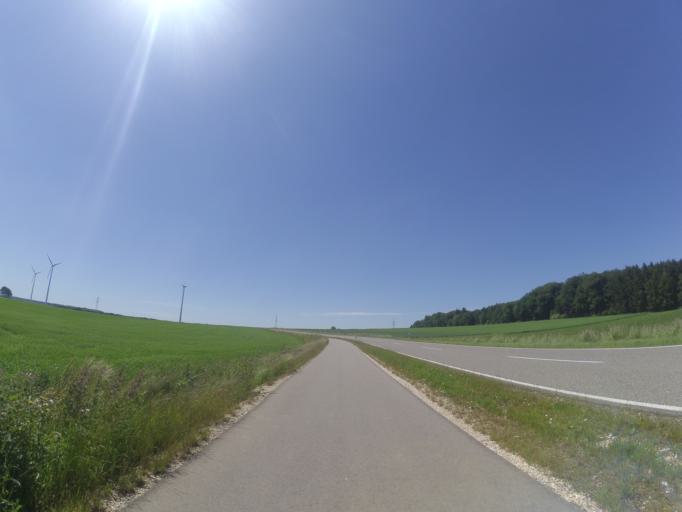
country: DE
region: Baden-Wuerttemberg
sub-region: Tuebingen Region
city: Nellingen
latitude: 48.4799
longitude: 9.8529
